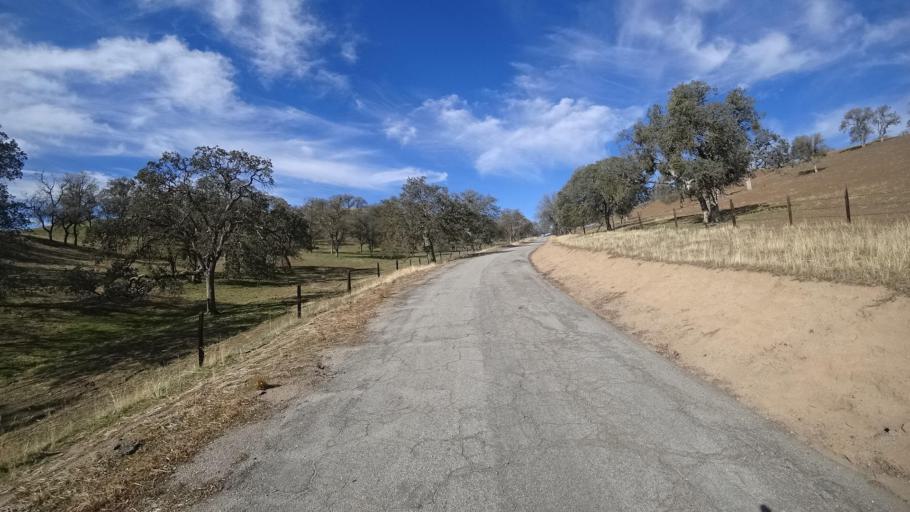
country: US
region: California
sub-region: Kern County
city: Oildale
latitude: 35.5644
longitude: -118.7955
